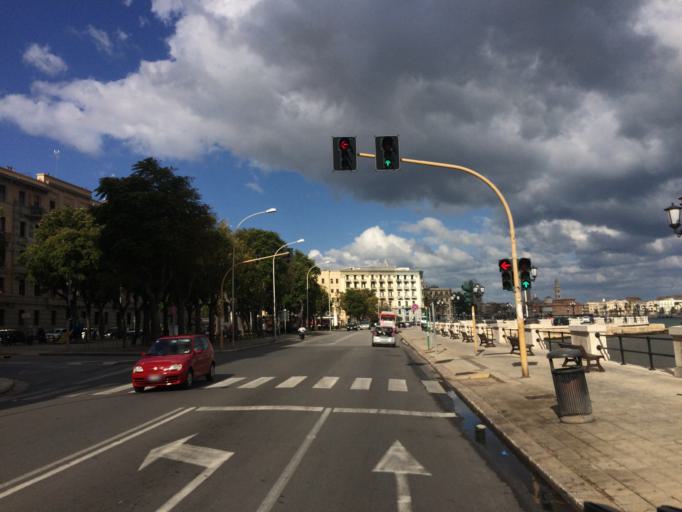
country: IT
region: Apulia
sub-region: Provincia di Bari
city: Bari
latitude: 41.1222
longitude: 16.8801
